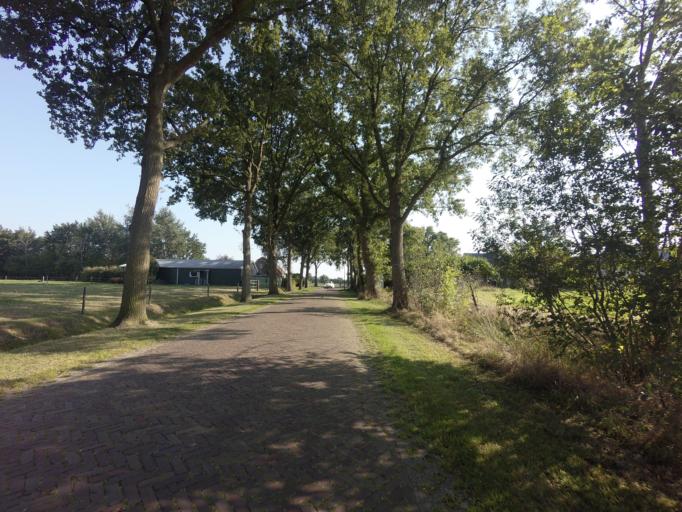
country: NL
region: Groningen
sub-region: Gemeente Zuidhorn
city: Aduard
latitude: 53.1696
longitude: 6.4775
